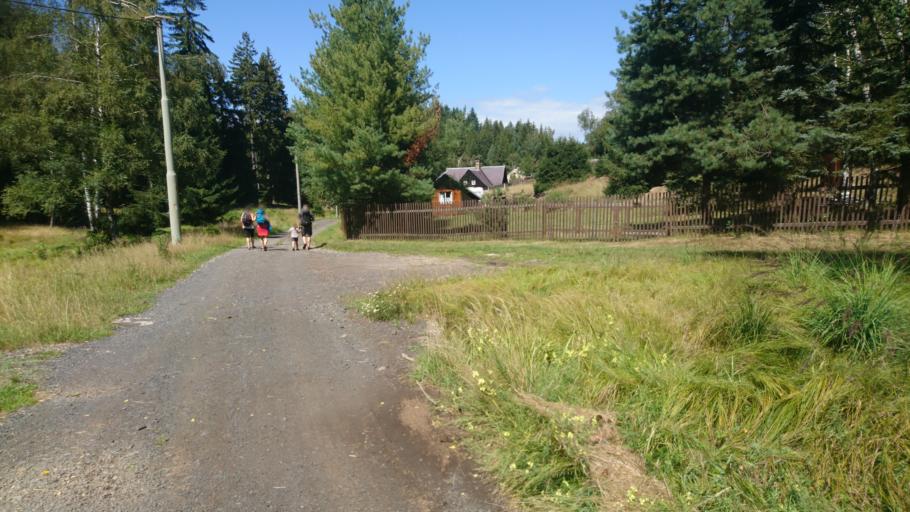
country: CZ
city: Kamenicky Senov
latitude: 50.8083
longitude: 14.4991
